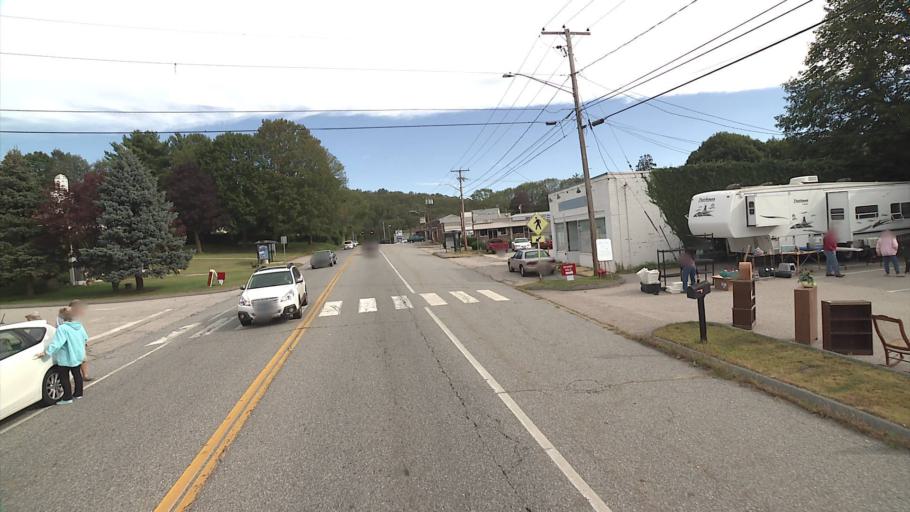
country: US
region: Connecticut
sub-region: New London County
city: Uncasville
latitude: 41.4344
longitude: -72.1098
